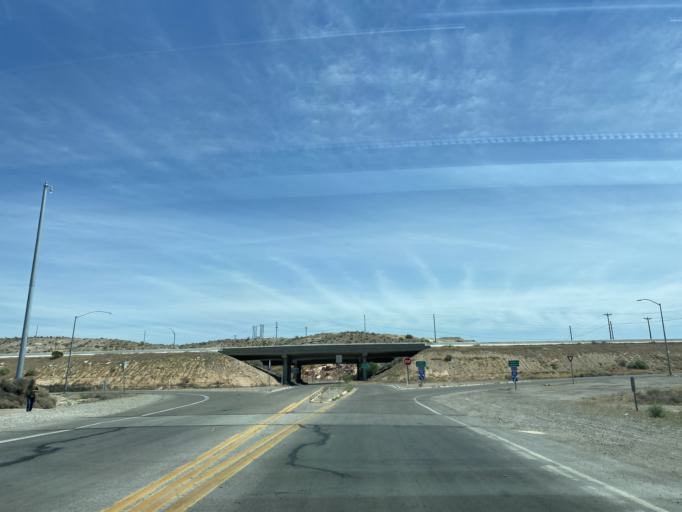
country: US
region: Nevada
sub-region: Clark County
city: Moapa Town
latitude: 36.6613
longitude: -114.5752
